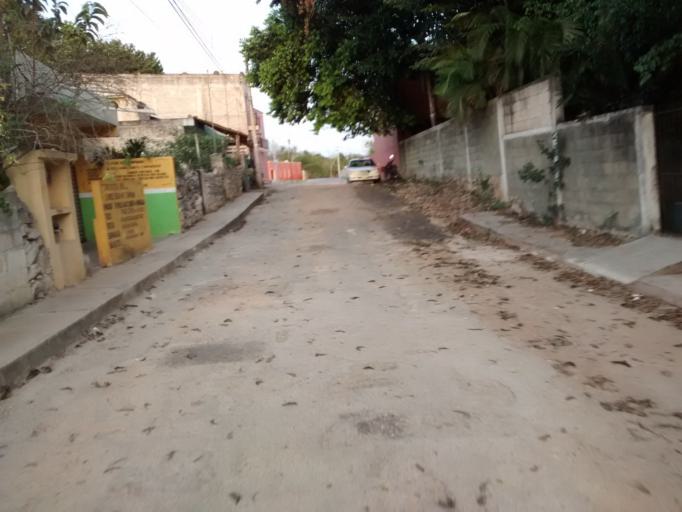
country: MX
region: Yucatan
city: Valladolid
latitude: 20.6811
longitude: -88.1861
